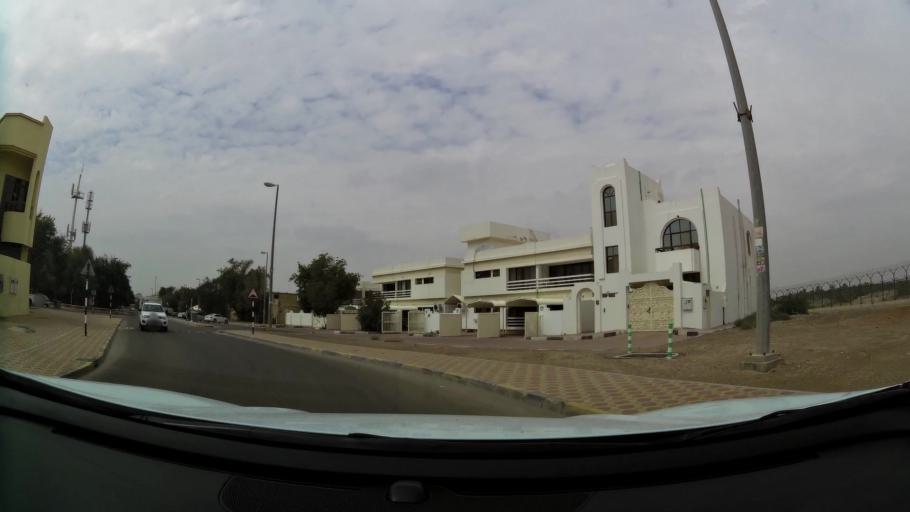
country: OM
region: Al Buraimi
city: Al Buraymi
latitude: 24.2278
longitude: 55.7865
